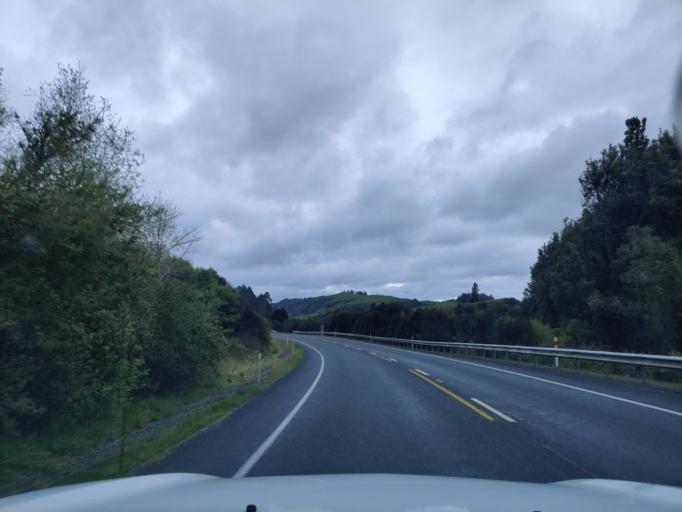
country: NZ
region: Waikato
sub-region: Otorohanga District
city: Otorohanga
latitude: -38.5036
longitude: 175.2045
